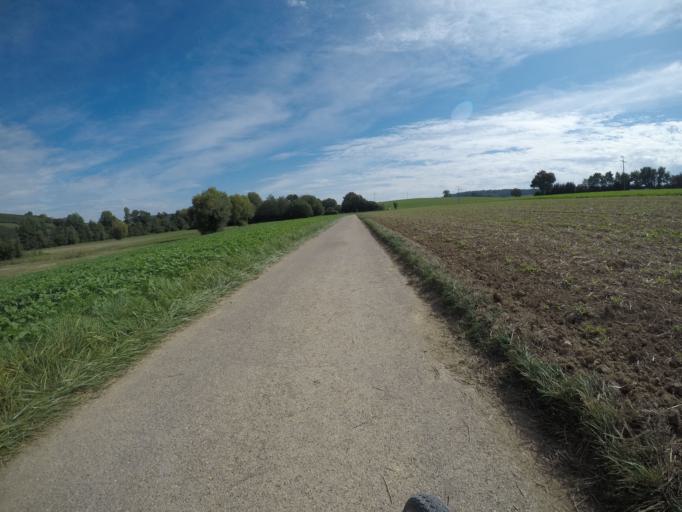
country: DE
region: Baden-Wuerttemberg
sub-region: Karlsruhe Region
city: Oberderdingen
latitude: 49.0761
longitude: 8.8213
